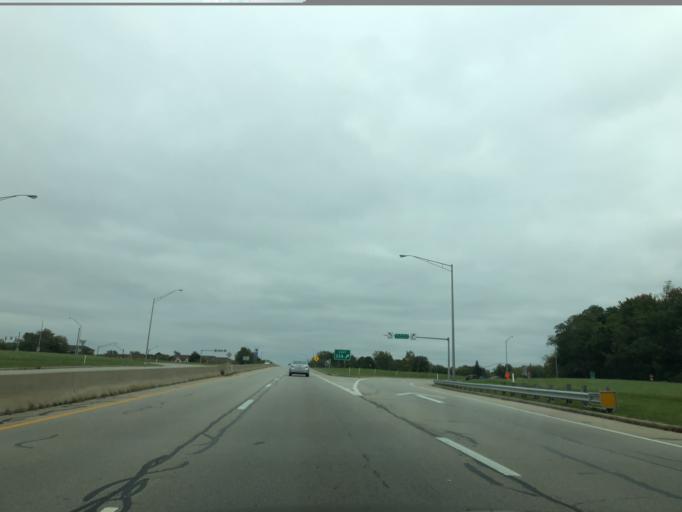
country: US
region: Ohio
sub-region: Hamilton County
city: Blue Ash
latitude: 39.2249
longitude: -84.3815
